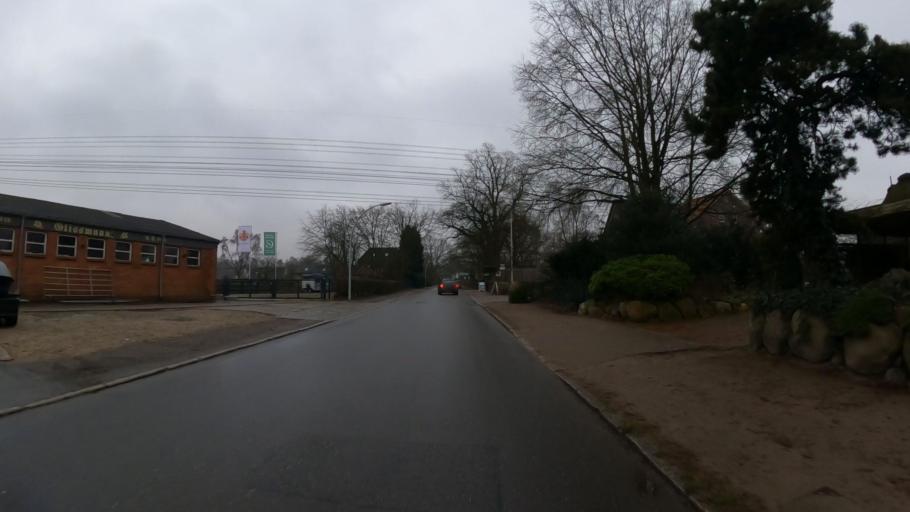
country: DE
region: Schleswig-Holstein
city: Rellingen
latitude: 53.5840
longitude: 9.7945
